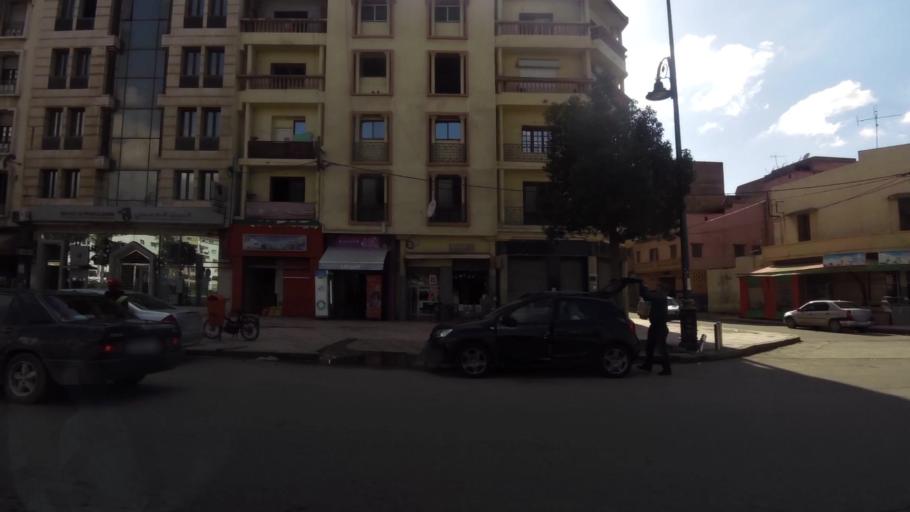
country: MA
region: Chaouia-Ouardigha
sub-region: Settat Province
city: Berrechid
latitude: 33.2684
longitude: -7.5846
